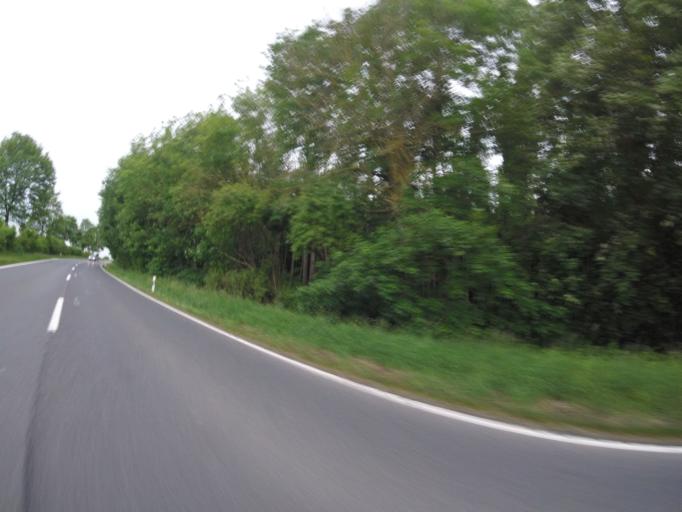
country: DE
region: Bavaria
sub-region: Upper Bavaria
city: Fahrenzhausen
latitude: 48.3682
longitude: 11.5485
